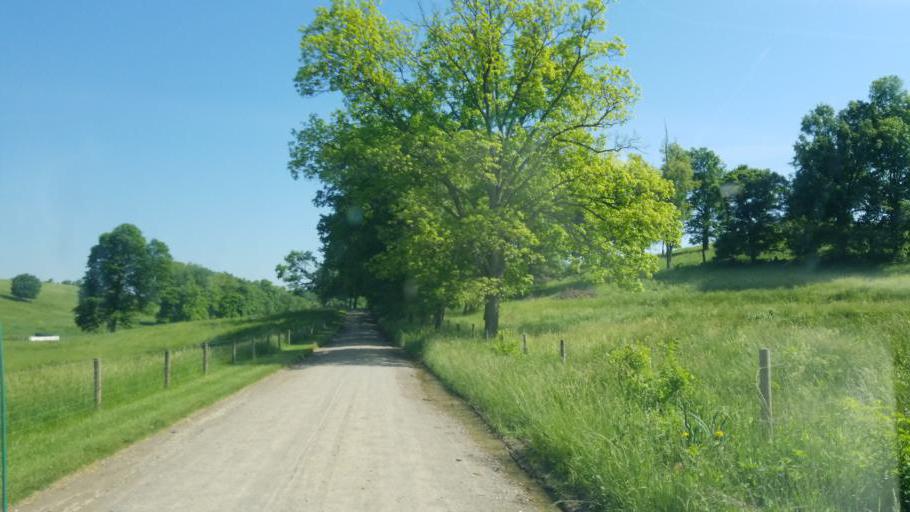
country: US
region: Ohio
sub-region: Holmes County
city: Millersburg
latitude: 40.4398
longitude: -81.8103
